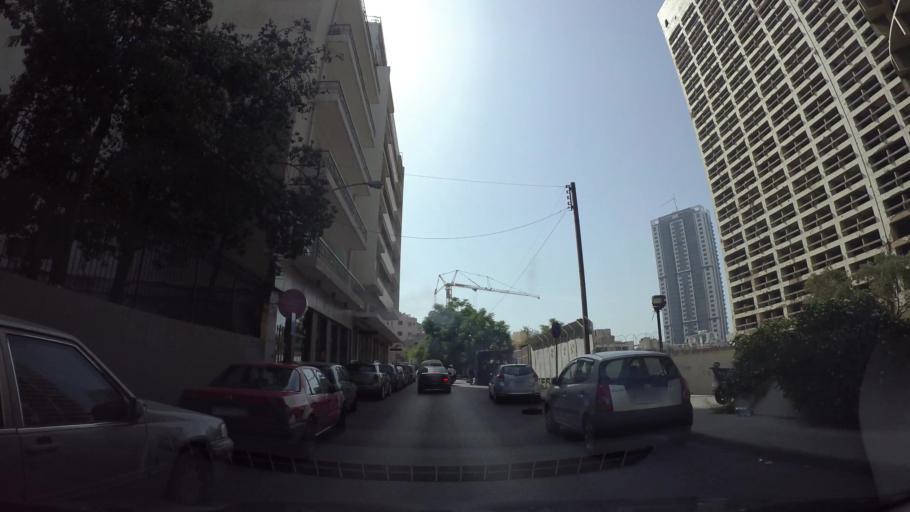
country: LB
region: Beyrouth
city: Beirut
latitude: 33.8991
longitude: 35.4949
